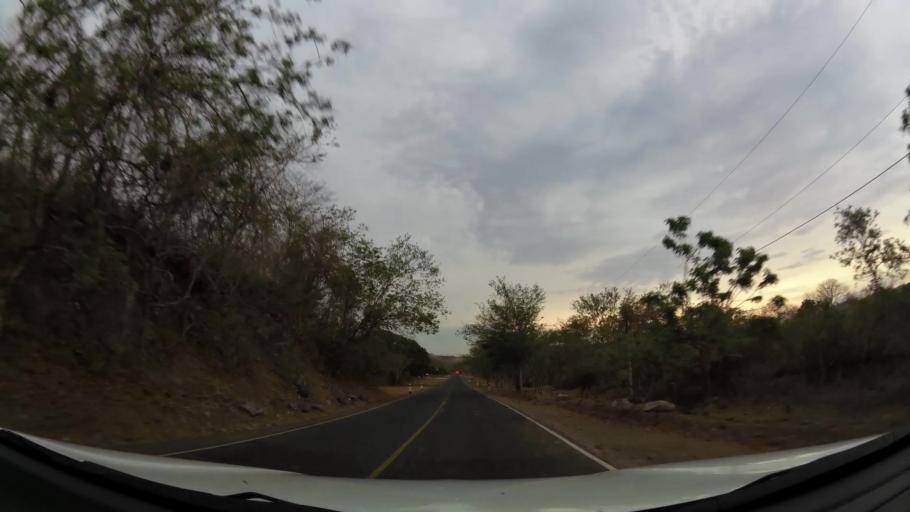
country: NI
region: Leon
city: La Jicaral
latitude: 12.7110
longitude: -86.3947
